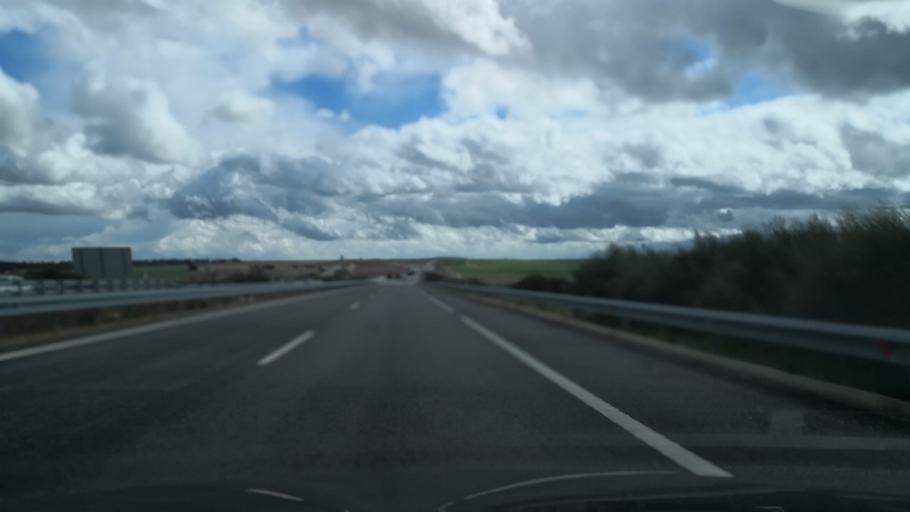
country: ES
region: Castille and Leon
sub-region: Provincia de Salamanca
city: Calzada de Valdunciel
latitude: 41.1371
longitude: -5.6971
